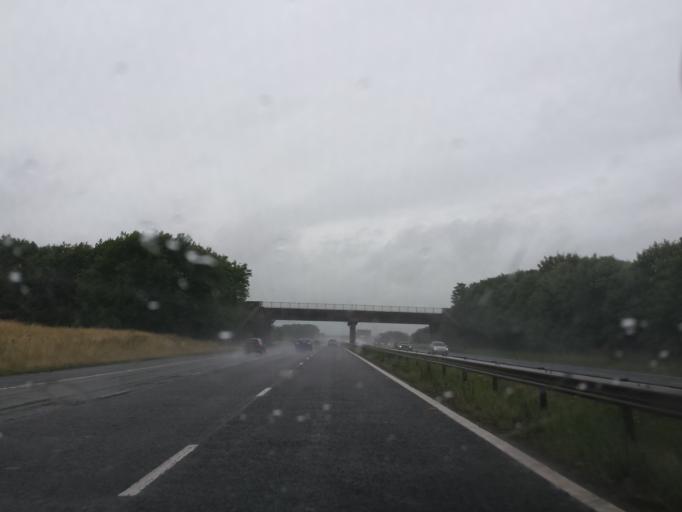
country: GB
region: England
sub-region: Doncaster
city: Stainton
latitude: 53.4621
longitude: -1.1921
